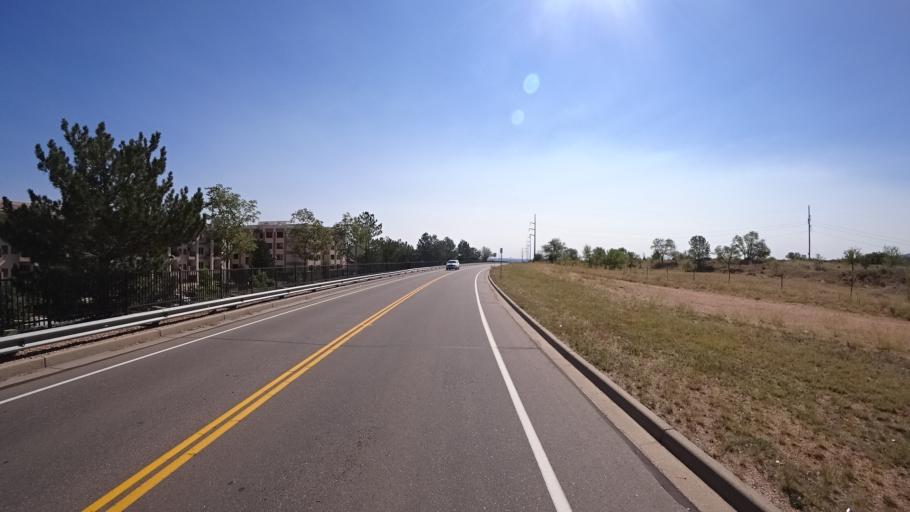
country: US
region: Colorado
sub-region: El Paso County
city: Colorado Springs
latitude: 38.8302
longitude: -104.8704
